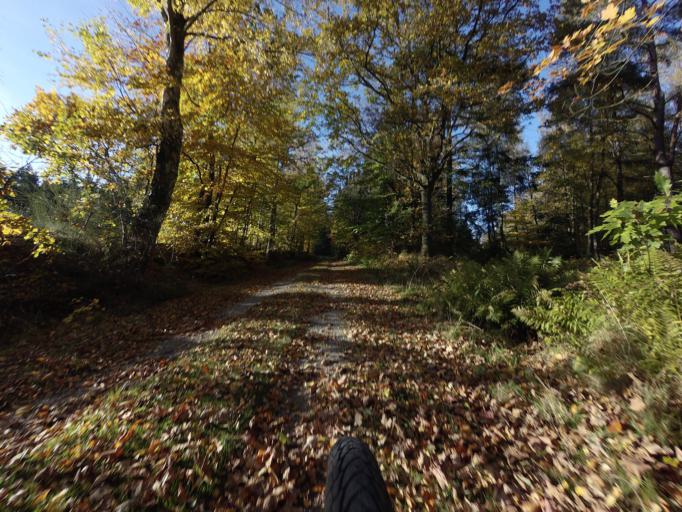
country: DK
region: Central Jutland
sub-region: Norddjurs Kommune
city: Grenaa
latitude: 56.5124
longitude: 10.8065
